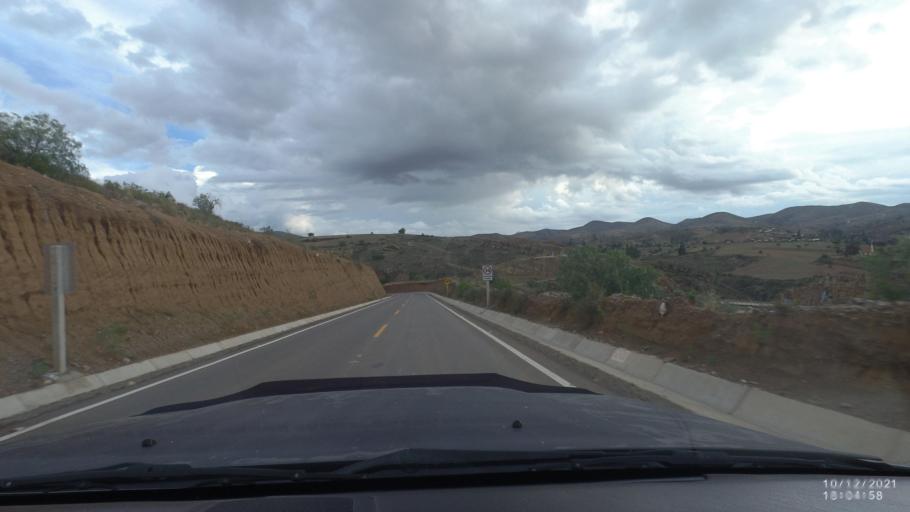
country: BO
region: Cochabamba
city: Cliza
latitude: -17.7730
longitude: -65.9261
